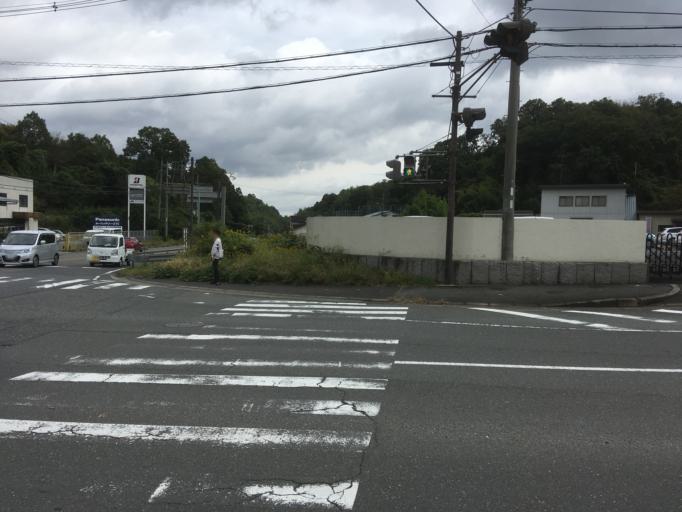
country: JP
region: Nara
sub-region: Ikoma-shi
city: Ikoma
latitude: 34.7297
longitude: 135.7312
